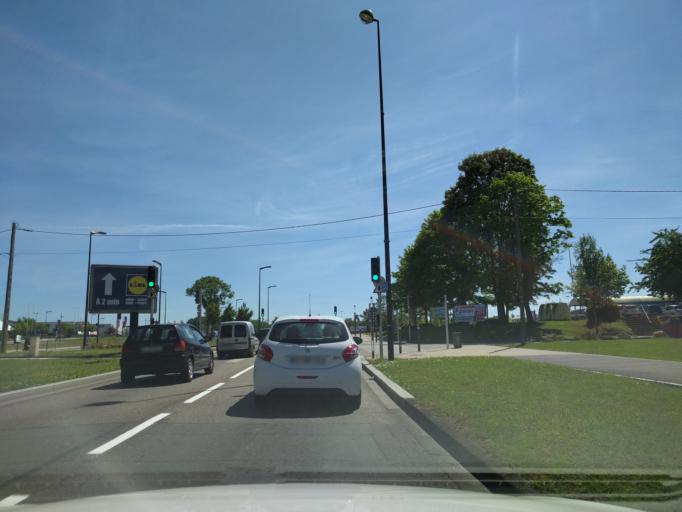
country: FR
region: Lorraine
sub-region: Departement de la Moselle
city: Peltre
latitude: 49.1072
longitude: 6.2258
